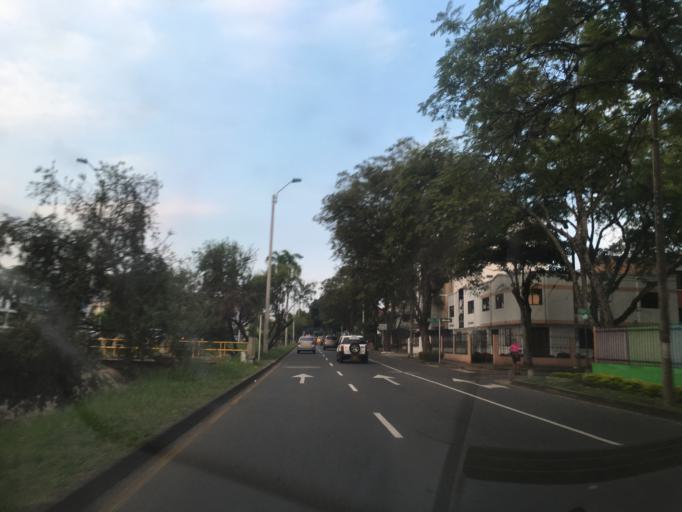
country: CO
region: Valle del Cauca
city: Cali
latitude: 3.3838
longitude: -76.5287
